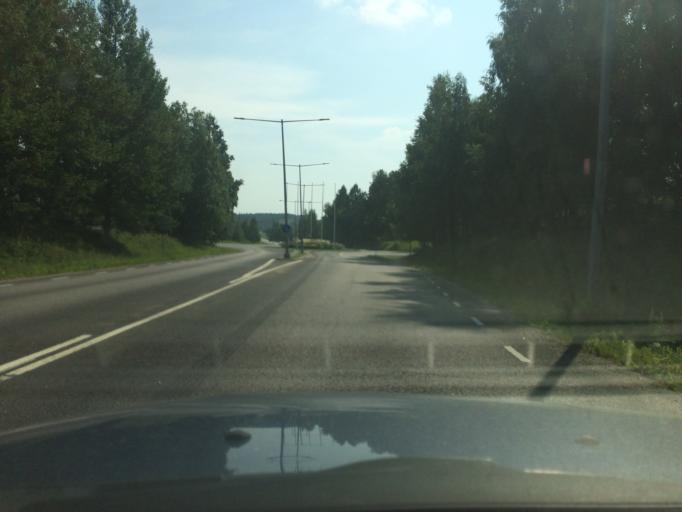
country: SE
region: Norrbotten
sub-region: Pitea Kommun
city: Pitea
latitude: 65.3256
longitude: 21.4785
